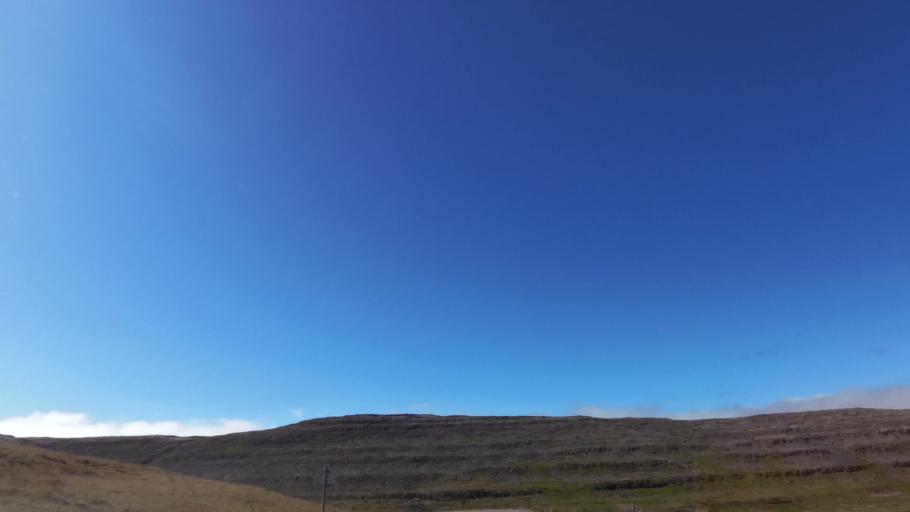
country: IS
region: West
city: Olafsvik
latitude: 65.5631
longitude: -24.1580
